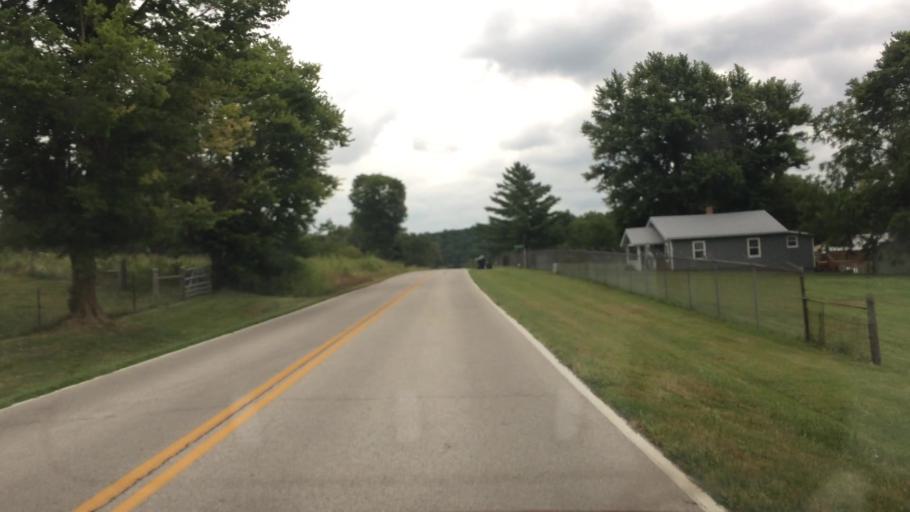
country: US
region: Missouri
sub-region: Greene County
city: Strafford
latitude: 37.2879
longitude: -93.0933
